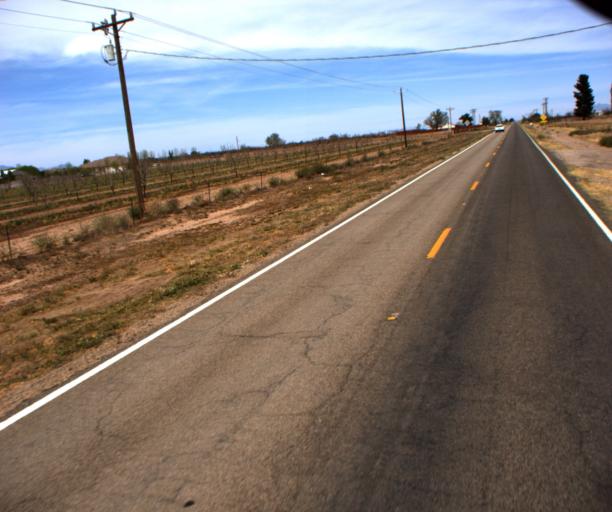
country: US
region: Arizona
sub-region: Cochise County
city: Bisbee
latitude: 31.7045
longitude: -109.6872
